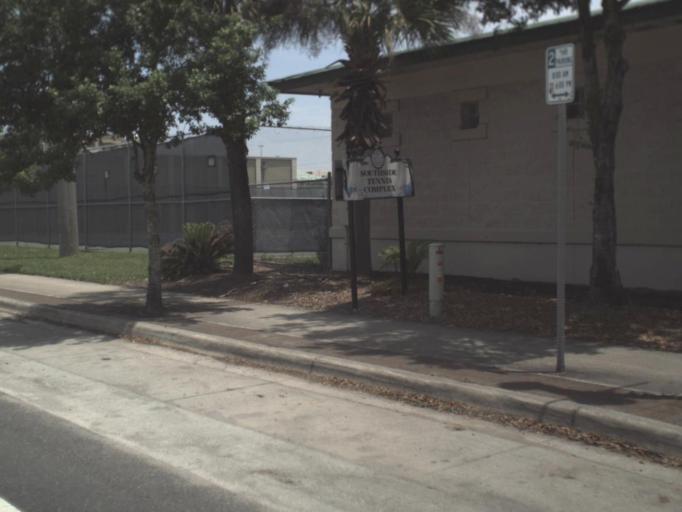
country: US
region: Florida
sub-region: Duval County
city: Jacksonville
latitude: 30.3097
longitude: -81.6547
